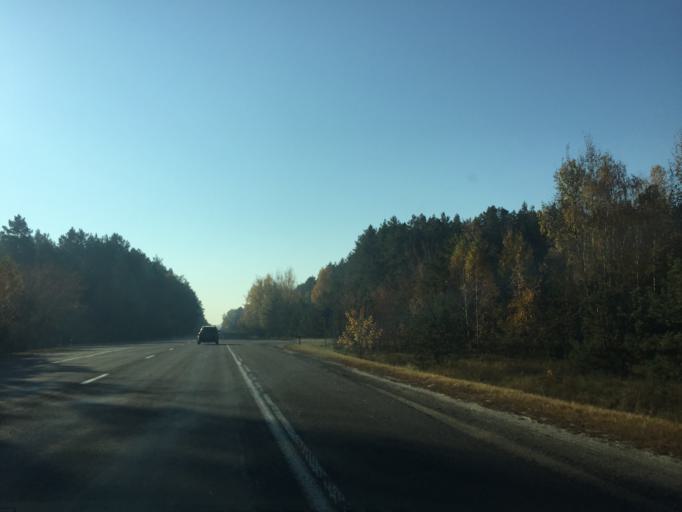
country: BY
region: Gomel
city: Kastsyukowka
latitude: 52.4347
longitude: 30.8266
